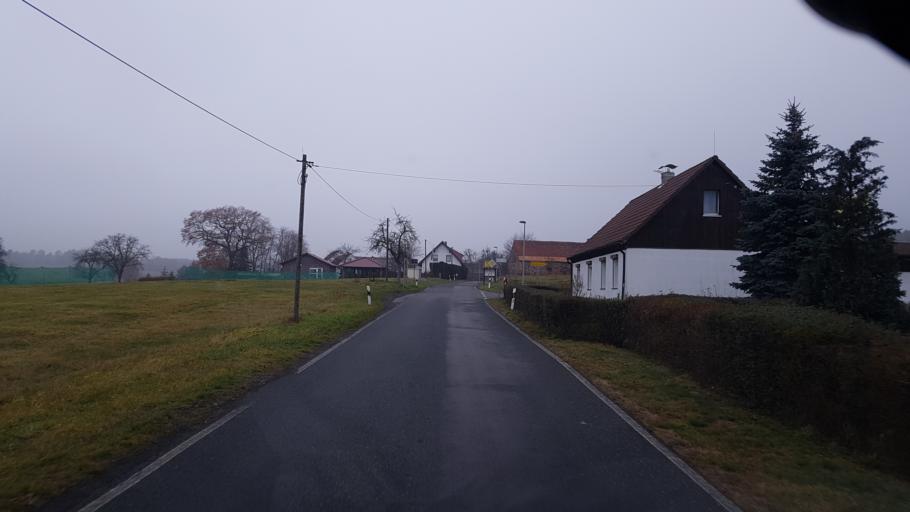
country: DE
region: Brandenburg
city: Calau
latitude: 51.6894
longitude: 13.9724
